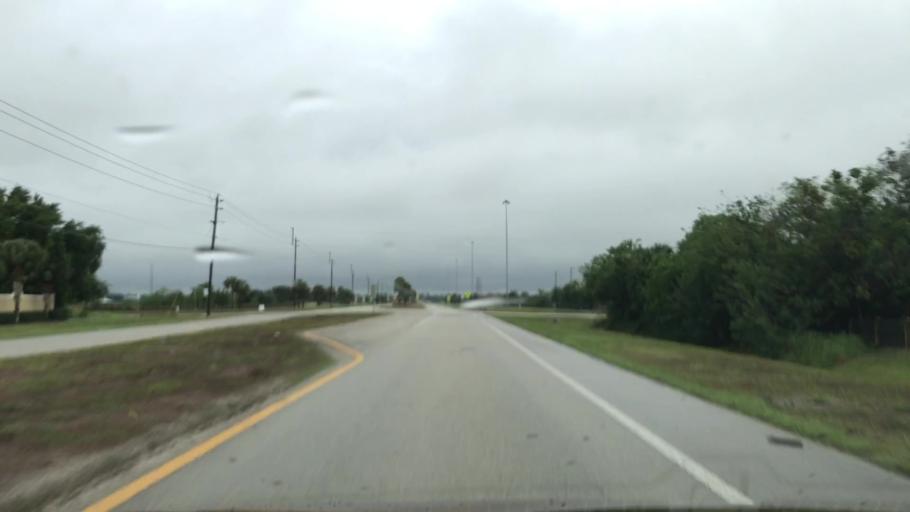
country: US
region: Florida
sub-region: Sarasota County
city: Fruitville
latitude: 27.3249
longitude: -82.4309
